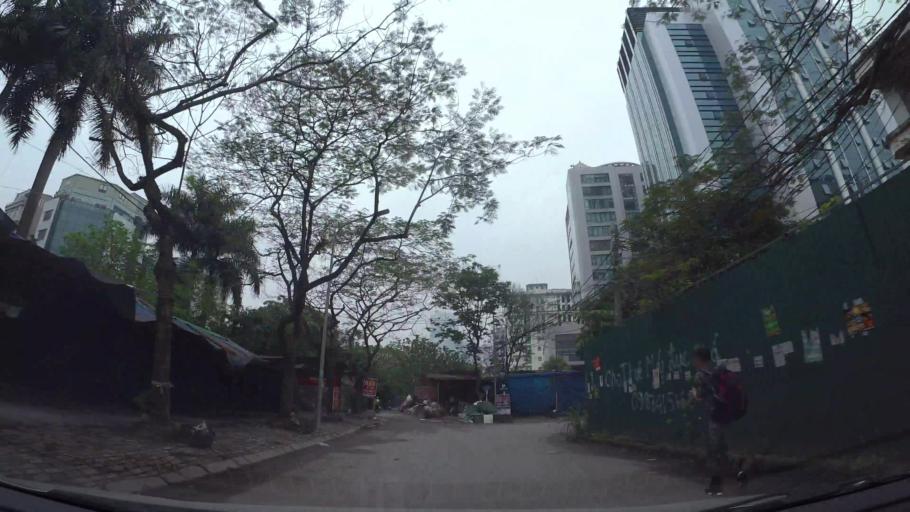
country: VN
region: Ha Noi
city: Cau Giay
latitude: 21.0301
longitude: 105.7834
